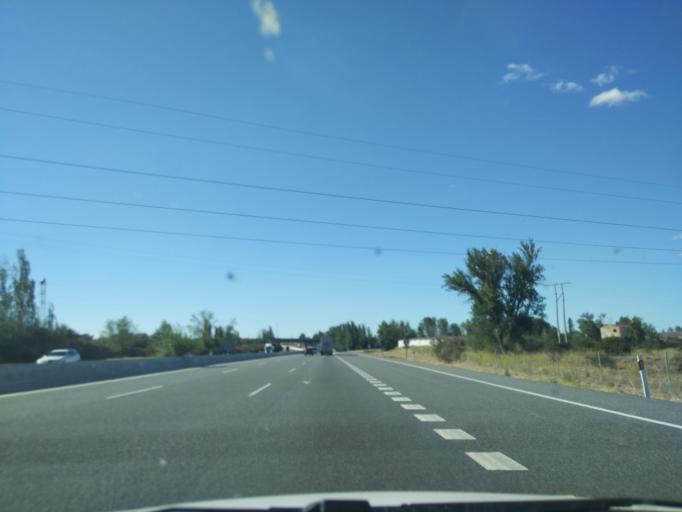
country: ES
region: Castille and Leon
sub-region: Provincia de Zamora
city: Benavente
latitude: 42.0129
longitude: -5.6642
